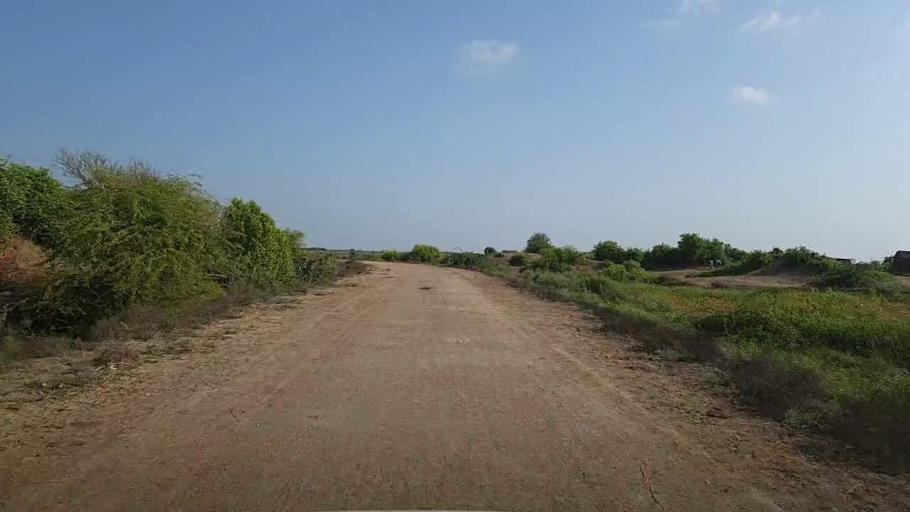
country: PK
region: Sindh
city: Kario
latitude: 24.7902
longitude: 68.6881
